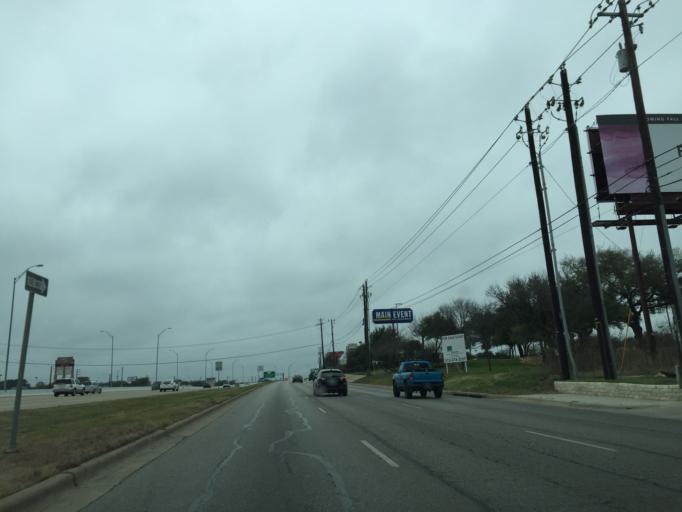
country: US
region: Texas
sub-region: Williamson County
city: Jollyville
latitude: 30.4436
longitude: -97.7850
